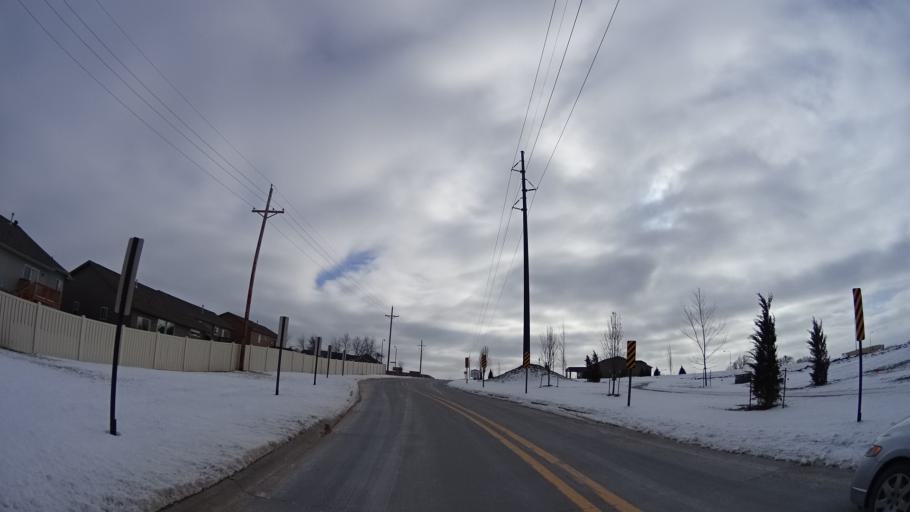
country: US
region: Nebraska
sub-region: Sarpy County
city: Offutt Air Force Base
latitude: 41.1056
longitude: -95.9859
